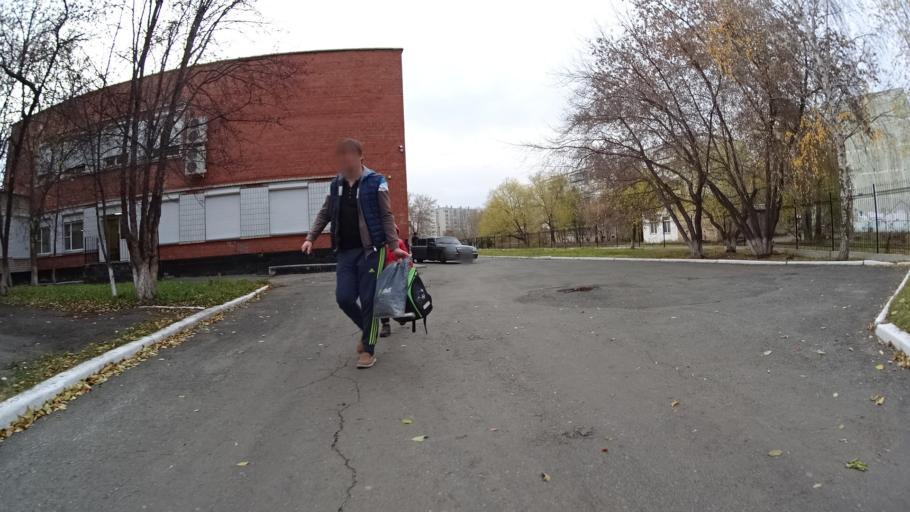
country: RU
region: Chelyabinsk
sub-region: Gorod Chelyabinsk
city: Chelyabinsk
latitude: 55.1919
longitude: 61.3101
